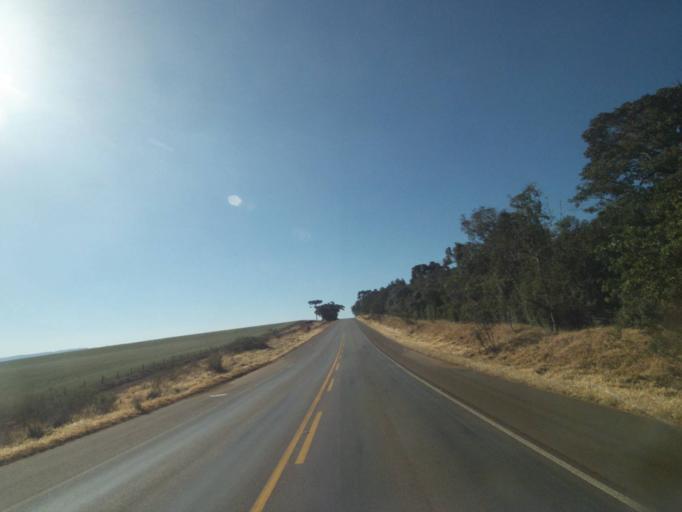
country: BR
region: Parana
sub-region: Tibagi
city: Tibagi
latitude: -24.7067
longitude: -50.4493
